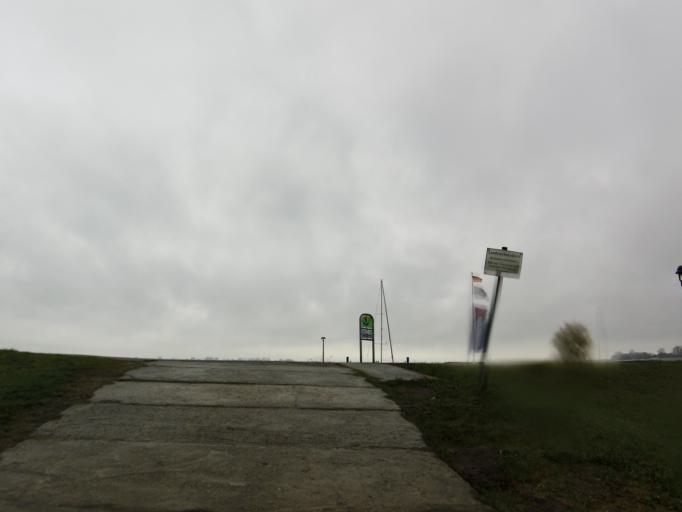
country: DE
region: Mecklenburg-Vorpommern
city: Zingst
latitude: 54.4326
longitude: 12.6975
